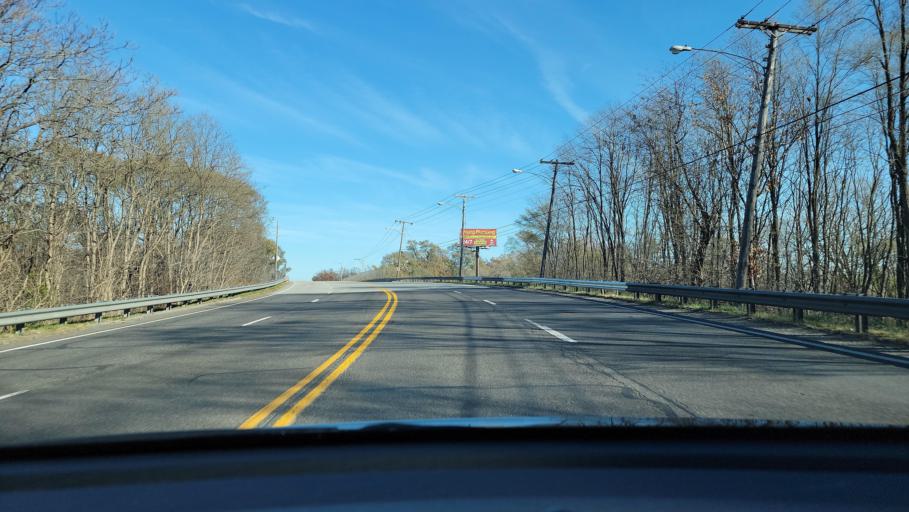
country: US
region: Indiana
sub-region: Porter County
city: Portage
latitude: 41.5906
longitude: -87.1979
